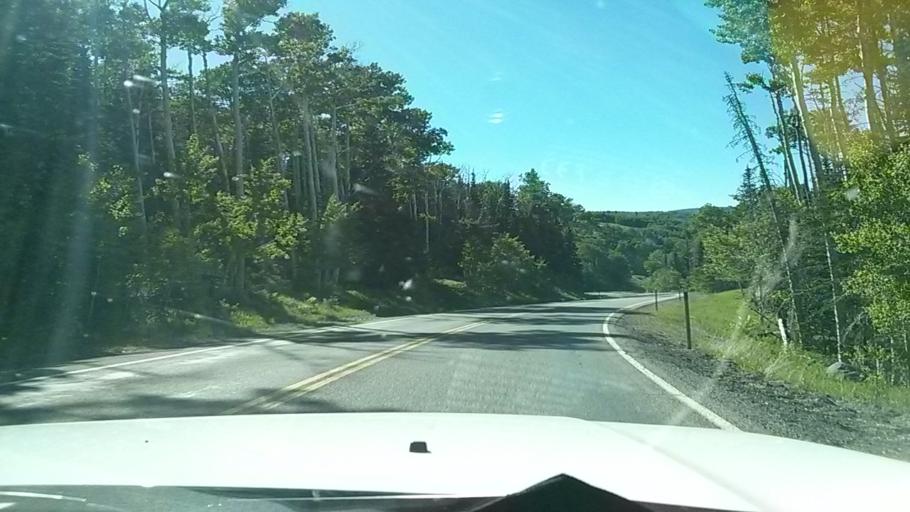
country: US
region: Utah
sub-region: Wayne County
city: Loa
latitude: 38.0695
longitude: -111.3332
